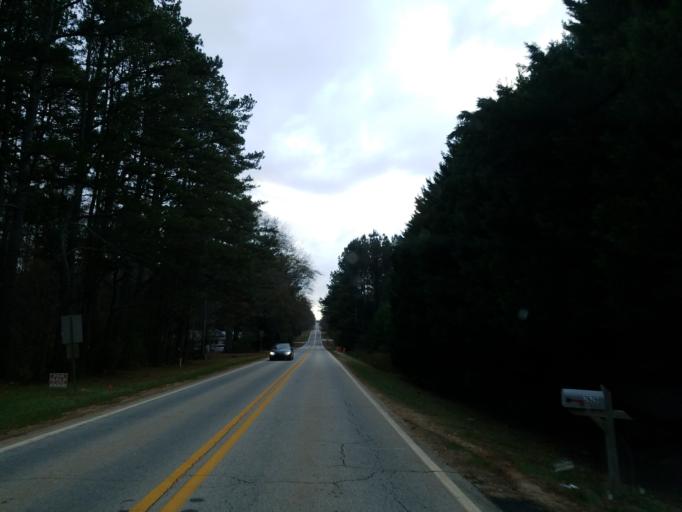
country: US
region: Georgia
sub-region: Dawson County
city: Dawsonville
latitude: 34.3360
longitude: -84.0656
